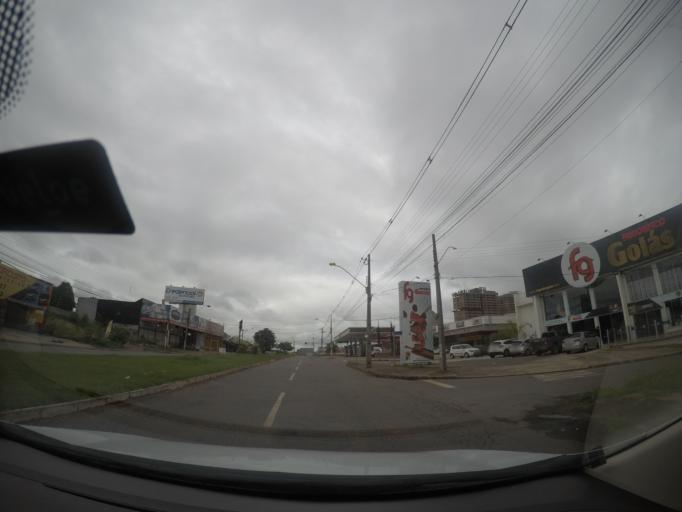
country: BR
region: Goias
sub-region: Goiania
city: Goiania
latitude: -16.7467
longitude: -49.3022
